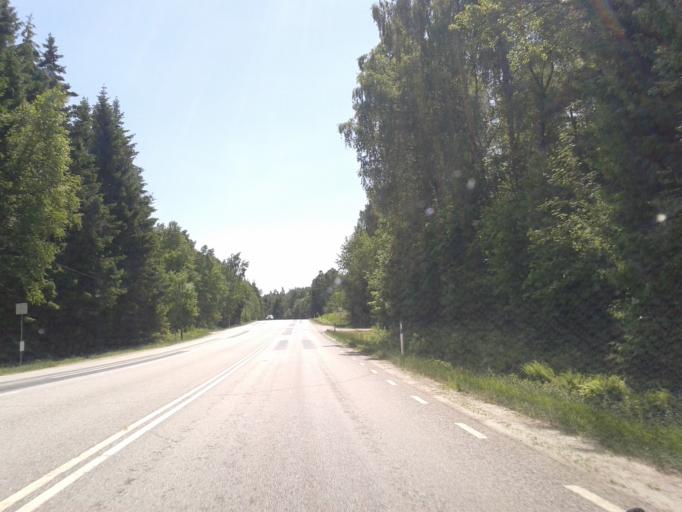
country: SE
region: Vaestra Goetaland
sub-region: Uddevalla Kommun
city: Ljungskile
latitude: 58.1198
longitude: 11.9855
